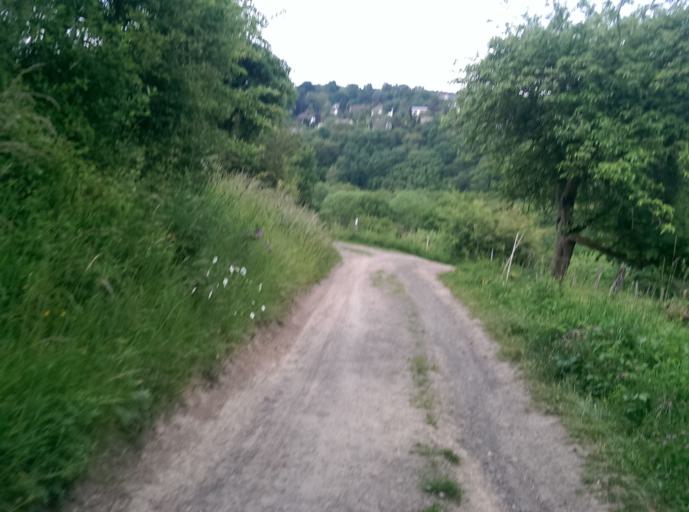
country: DE
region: Rheinland-Pfalz
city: Melsbach
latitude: 50.4750
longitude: 7.4715
